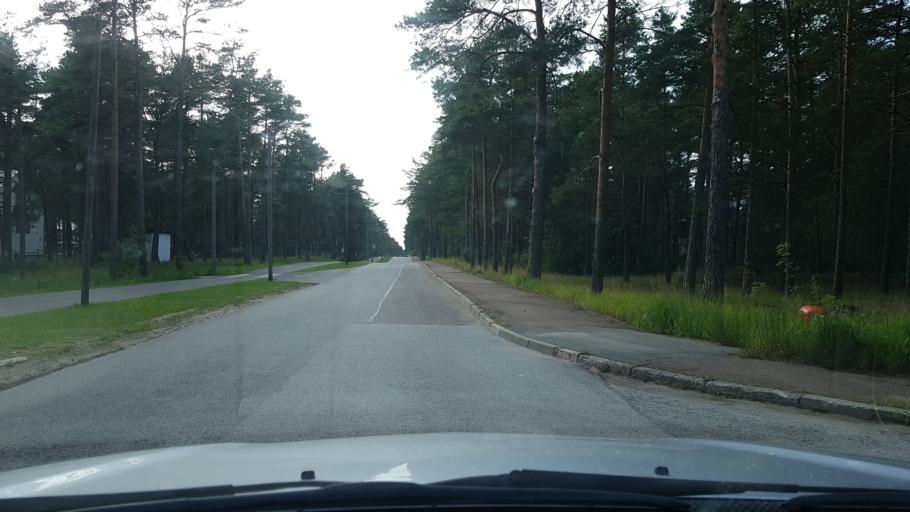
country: EE
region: Ida-Virumaa
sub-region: Narva-Joesuu linn
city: Narva-Joesuu
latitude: 59.4518
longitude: 28.0579
